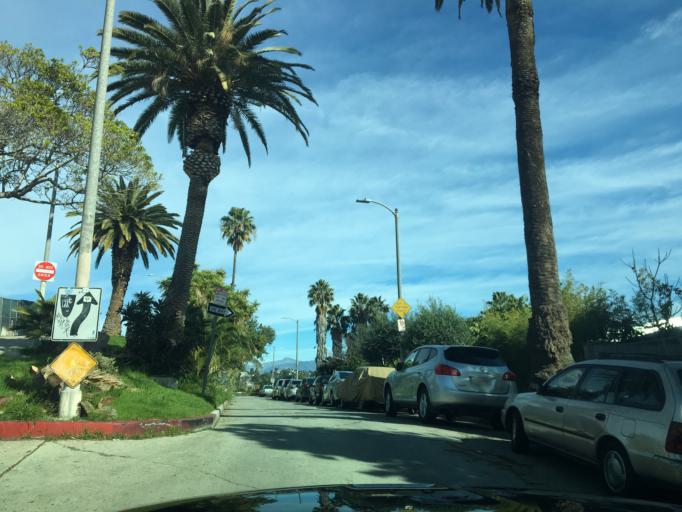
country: US
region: California
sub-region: Los Angeles County
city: Silver Lake
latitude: 34.0751
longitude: -118.2837
